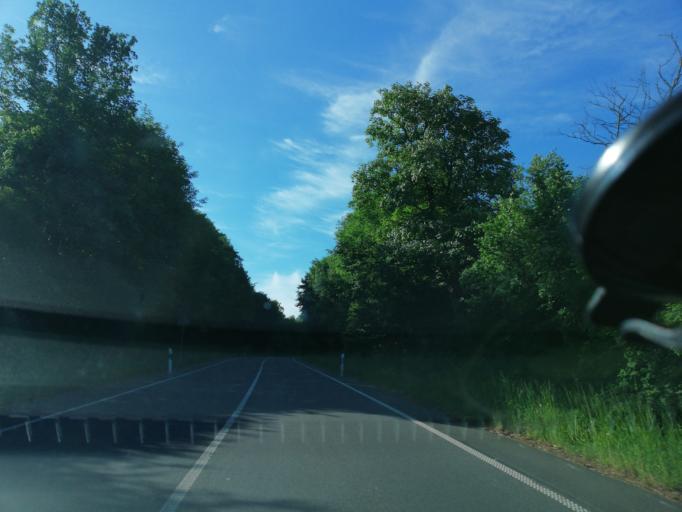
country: DE
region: North Rhine-Westphalia
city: Gevelsberg
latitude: 51.3660
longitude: 7.3269
